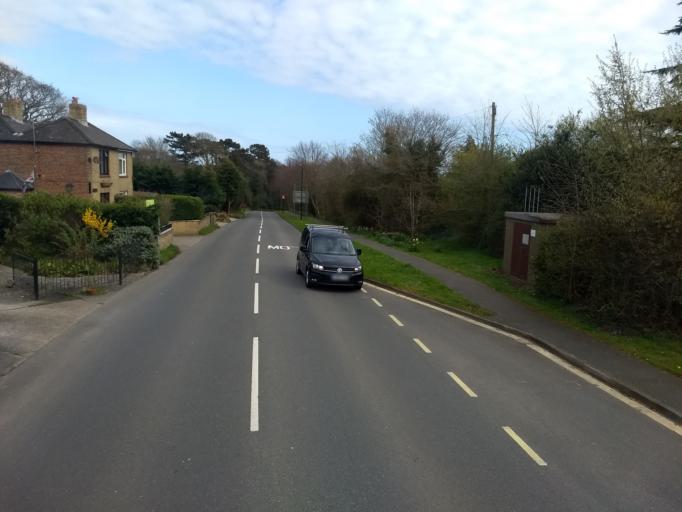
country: GB
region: England
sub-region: Isle of Wight
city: Seaview
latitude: 50.7180
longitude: -1.1289
